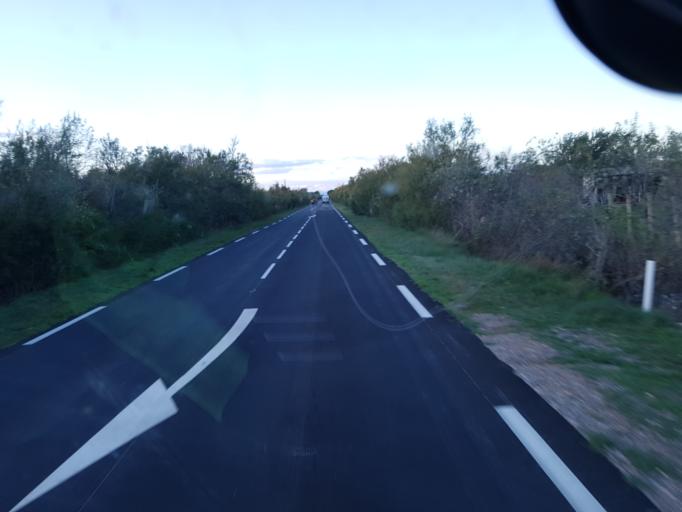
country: FR
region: Languedoc-Roussillon
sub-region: Departement de l'Aude
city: Port-la-Nouvelle
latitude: 42.9995
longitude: 3.0413
